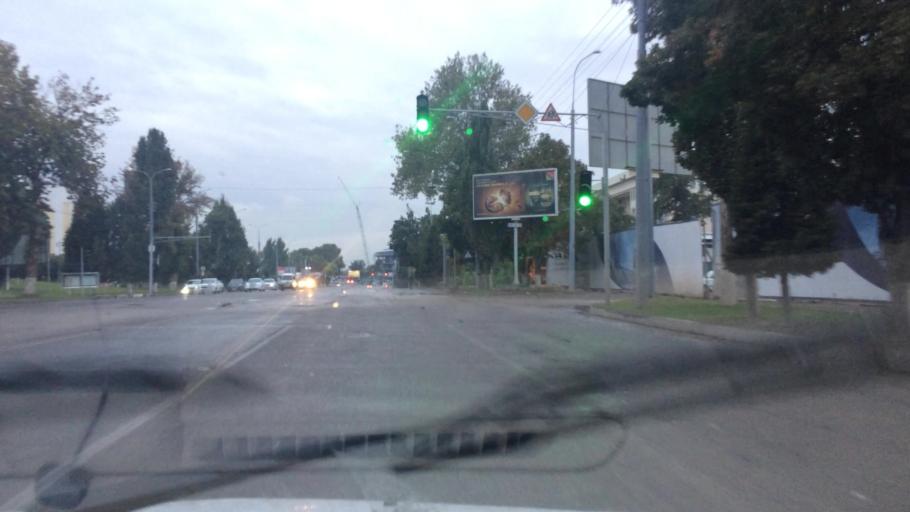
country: UZ
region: Toshkent Shahri
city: Tashkent
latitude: 41.3150
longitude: 69.2538
